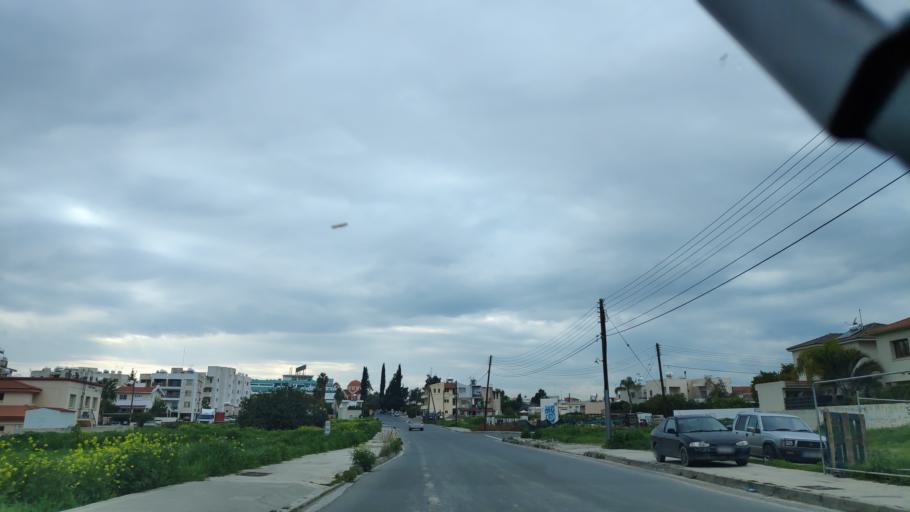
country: CY
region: Limassol
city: Limassol
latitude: 34.6950
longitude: 33.0198
